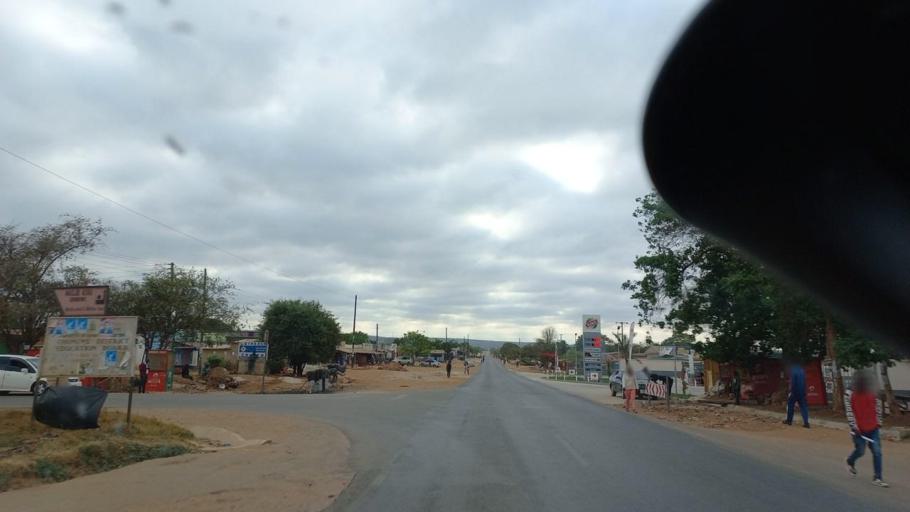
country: ZM
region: Lusaka
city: Chongwe
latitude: -15.3269
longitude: 28.6839
